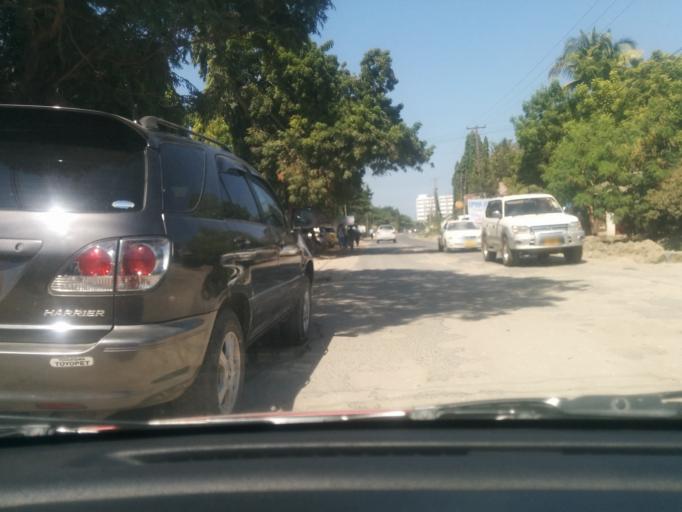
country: TZ
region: Dar es Salaam
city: Magomeni
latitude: -6.7734
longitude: 39.2250
